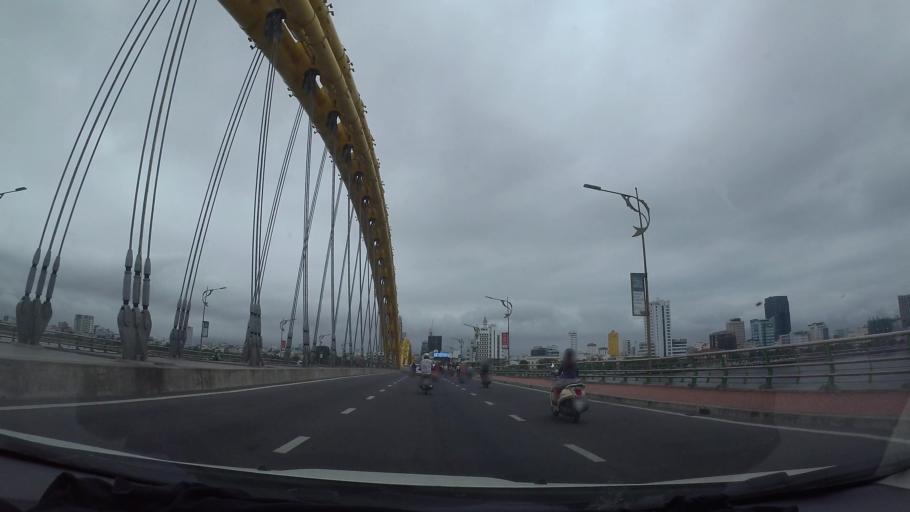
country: VN
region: Da Nang
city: Son Tra
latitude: 16.0611
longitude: 108.2275
